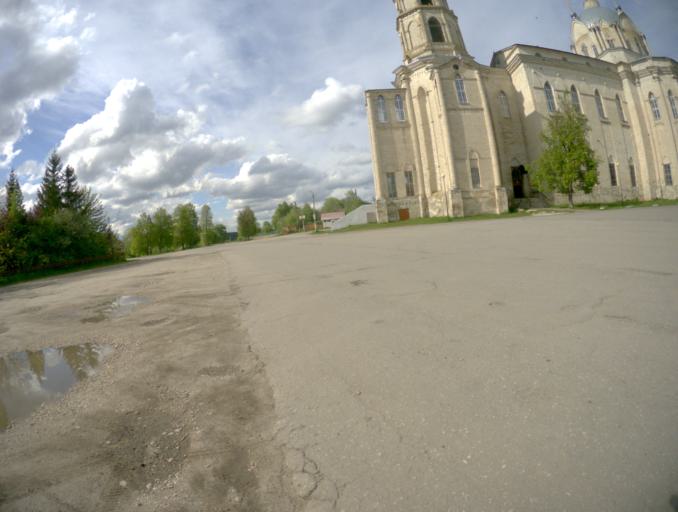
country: RU
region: Rjazan
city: Gus'-Zheleznyy
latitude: 55.0552
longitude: 41.1594
